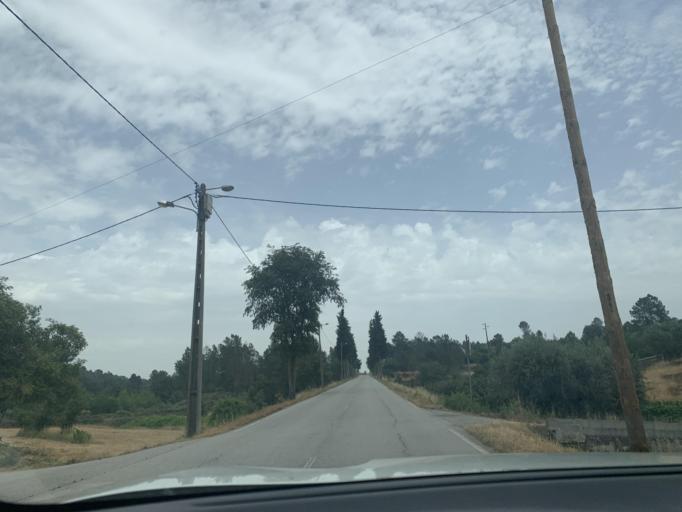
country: PT
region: Guarda
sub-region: Fornos de Algodres
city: Fornos de Algodres
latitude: 40.5810
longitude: -7.6298
